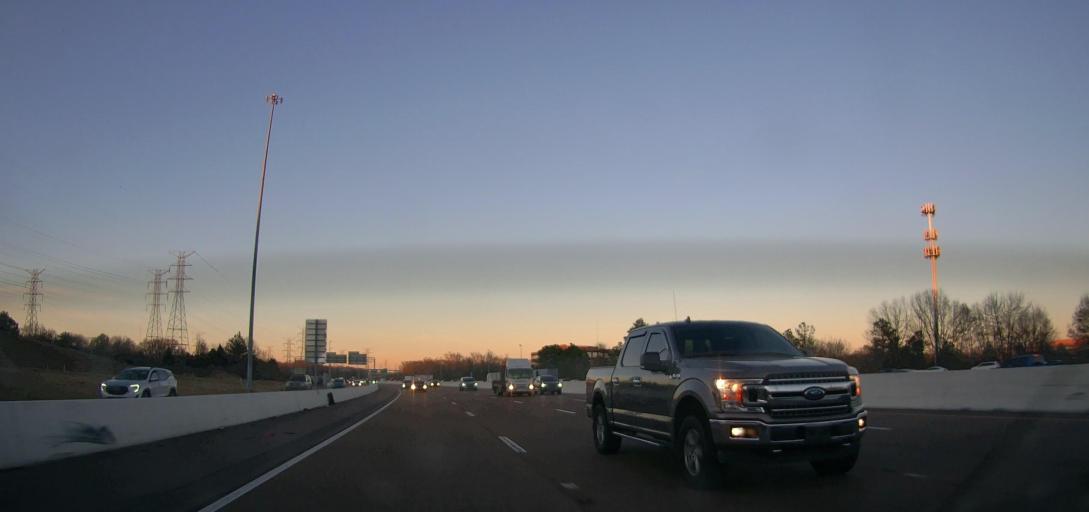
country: US
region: Tennessee
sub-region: Shelby County
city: Bartlett
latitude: 35.1313
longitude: -89.8688
